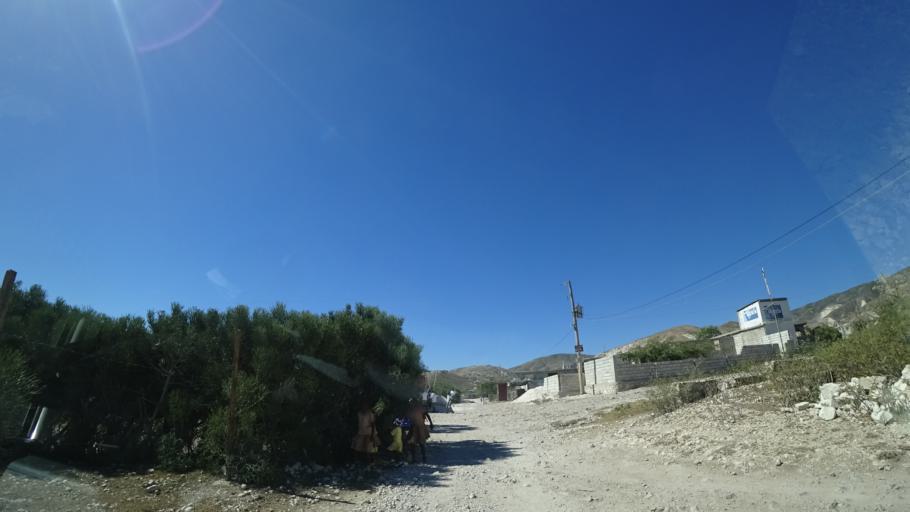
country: HT
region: Ouest
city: Croix des Bouquets
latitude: 18.6711
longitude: -72.2389
